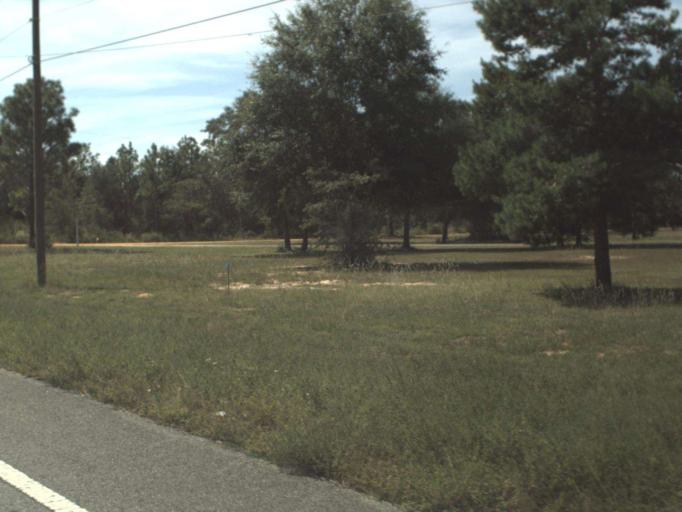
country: US
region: Florida
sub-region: Holmes County
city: Bonifay
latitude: 30.5356
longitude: -85.6404
